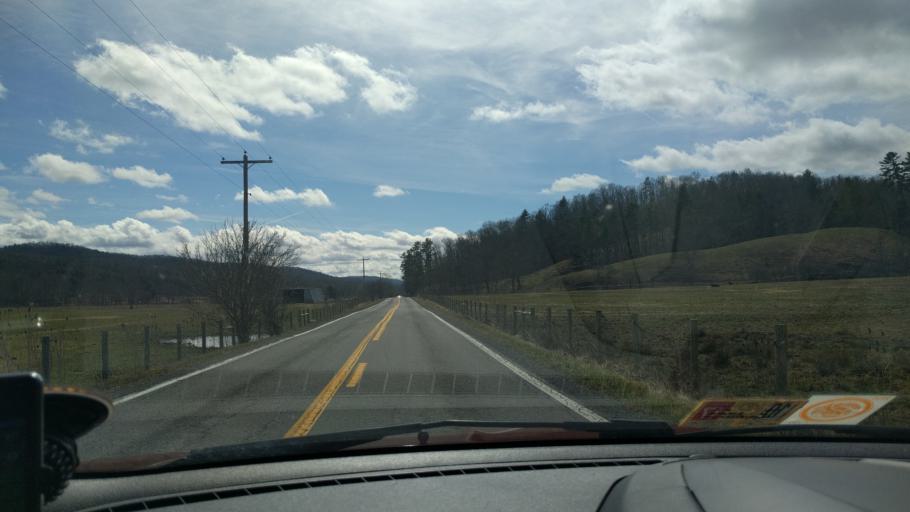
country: US
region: West Virginia
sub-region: Pocahontas County
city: Marlinton
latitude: 38.2318
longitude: -79.9087
